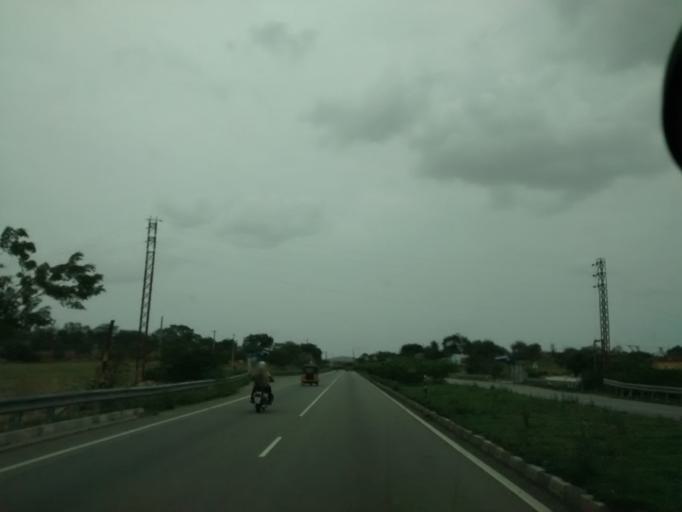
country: IN
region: Andhra Pradesh
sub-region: Kurnool
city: Ramapuram
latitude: 15.1919
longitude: 77.6980
